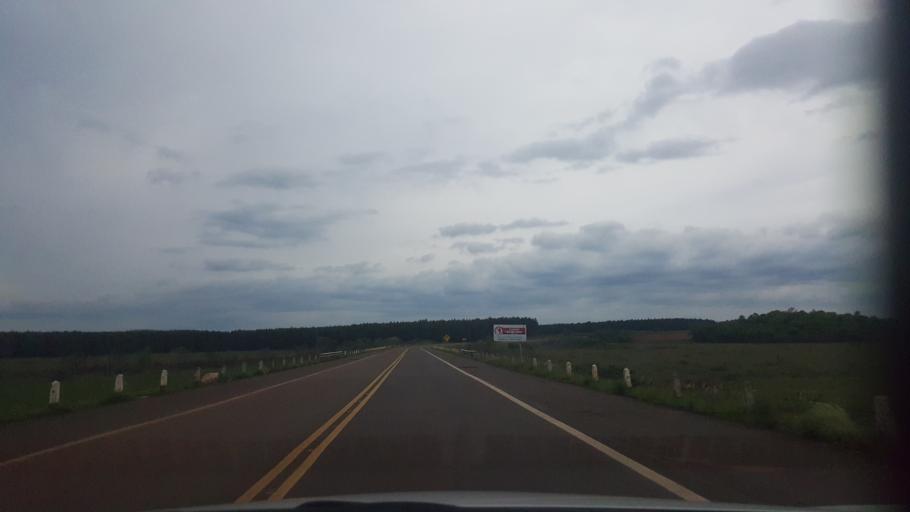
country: AR
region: Misiones
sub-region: Departamento de Candelaria
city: Candelaria
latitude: -27.4906
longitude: -55.7402
